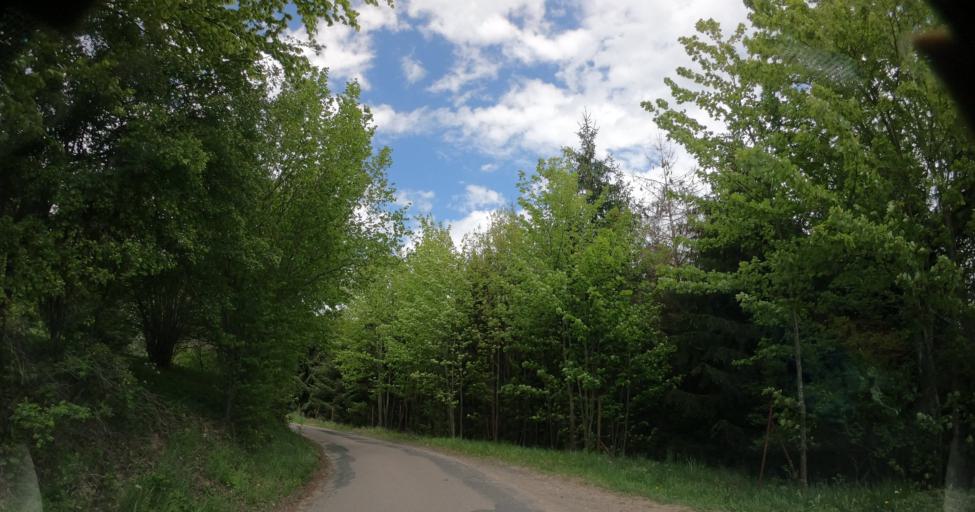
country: PL
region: West Pomeranian Voivodeship
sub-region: Powiat drawski
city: Drawsko Pomorskie
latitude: 53.5688
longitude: 15.7633
